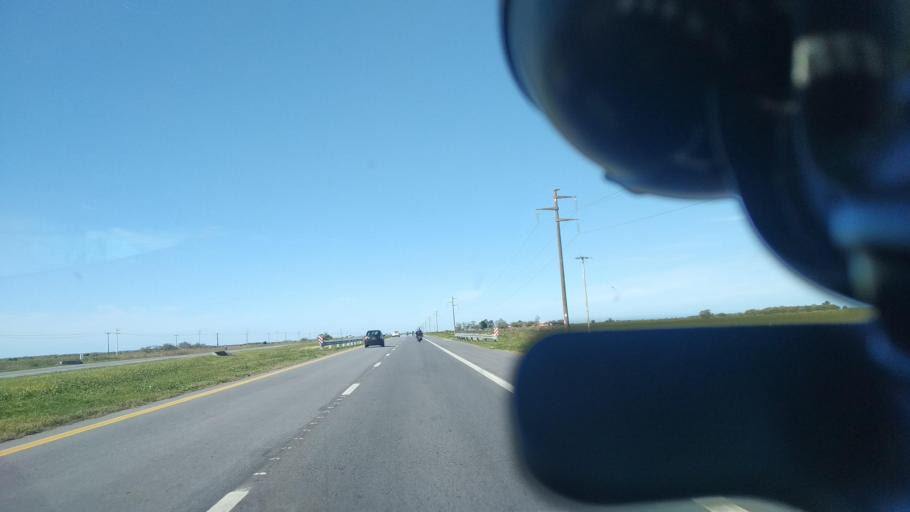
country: AR
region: Buenos Aires
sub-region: Partido de General Lavalle
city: General Lavalle
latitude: -36.4285
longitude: -56.8813
